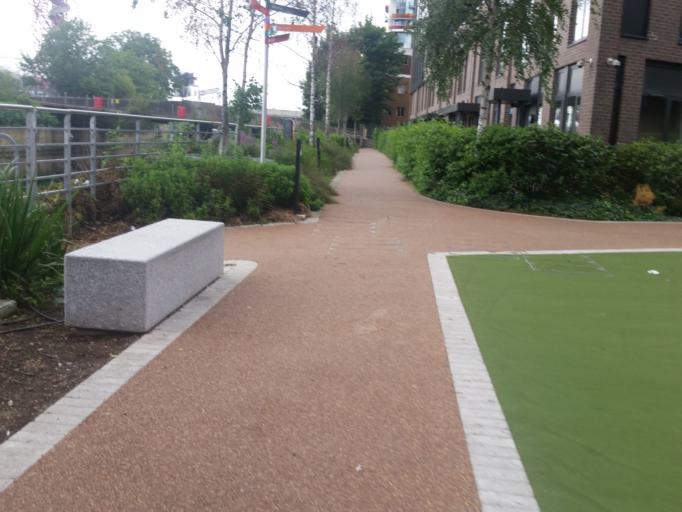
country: GB
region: England
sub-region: Greater London
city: Poplar
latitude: 51.5355
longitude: -0.0072
